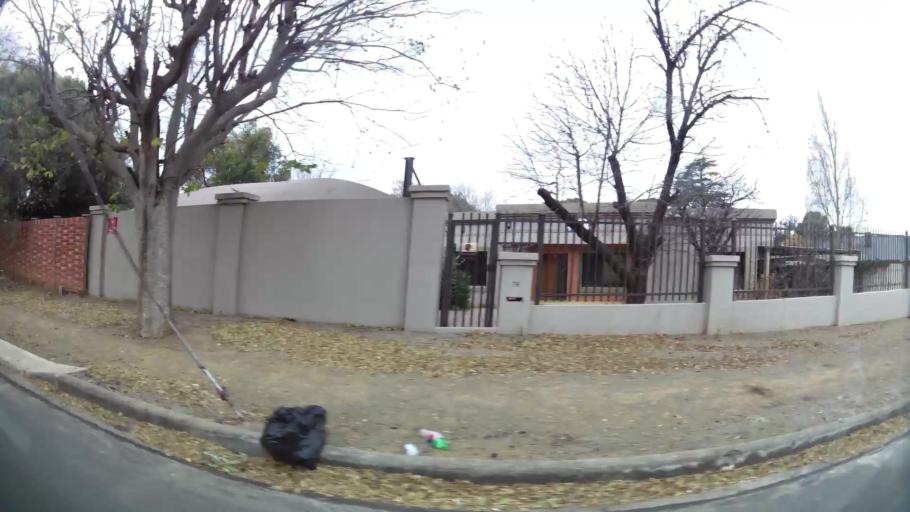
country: ZA
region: Orange Free State
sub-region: Mangaung Metropolitan Municipality
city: Bloemfontein
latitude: -29.0872
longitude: 26.2048
